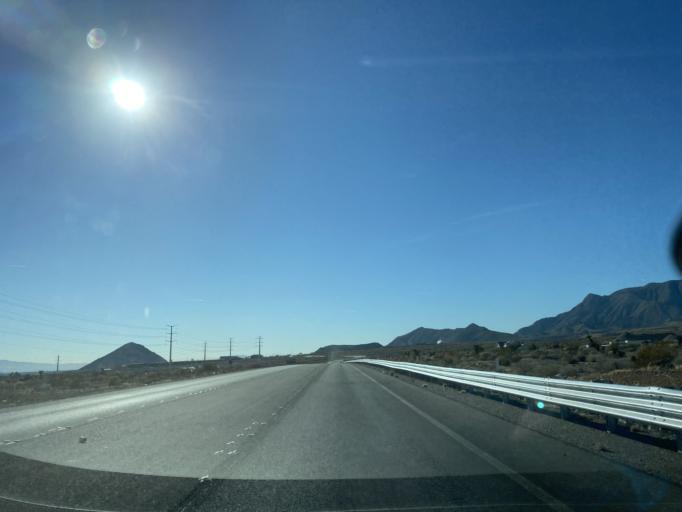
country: US
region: Nevada
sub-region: Clark County
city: Summerlin South
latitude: 36.2692
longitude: -115.3301
